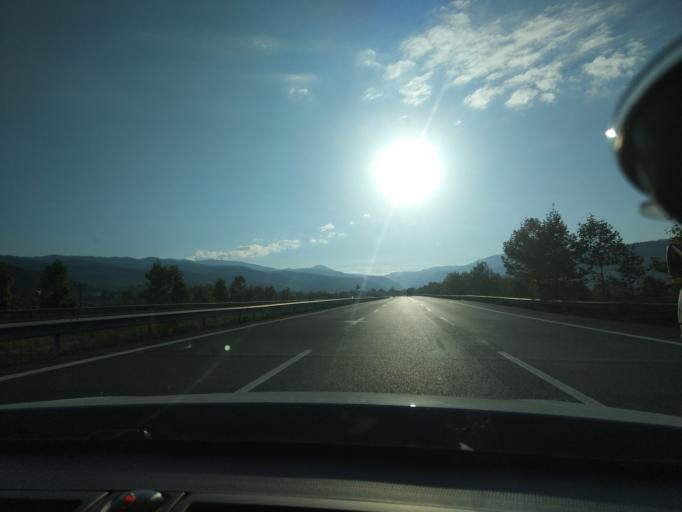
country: TR
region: Duzce
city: Kaynasli
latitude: 40.7812
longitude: 31.3190
